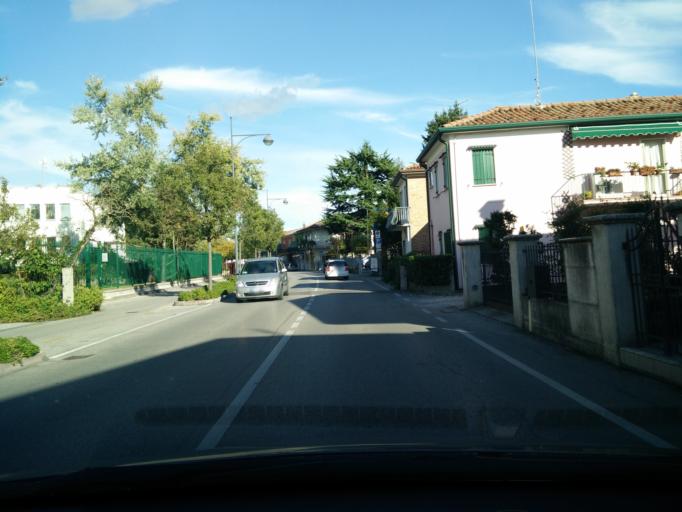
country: IT
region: Veneto
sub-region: Provincia di Venezia
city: San Dona di Piave
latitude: 45.6321
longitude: 12.5711
